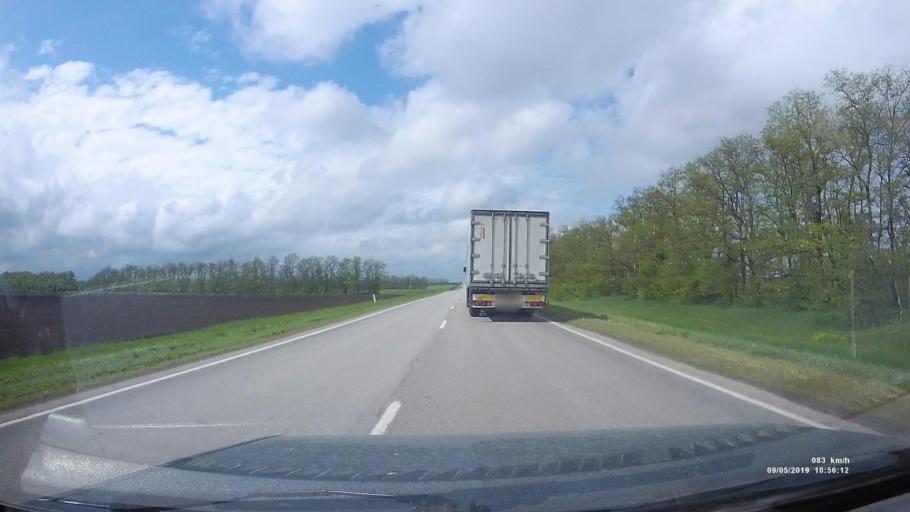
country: RU
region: Rostov
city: Peshkovo
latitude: 46.8701
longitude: 39.3029
